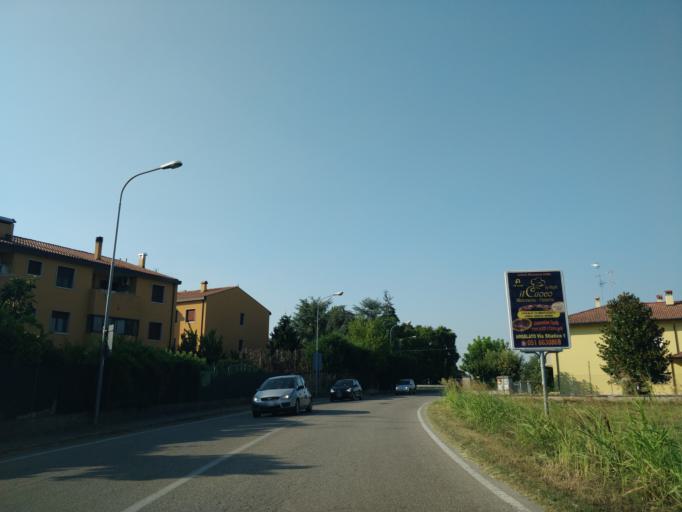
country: IT
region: Emilia-Romagna
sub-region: Provincia di Bologna
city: Castello d'Argile
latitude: 44.6801
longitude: 11.3013
